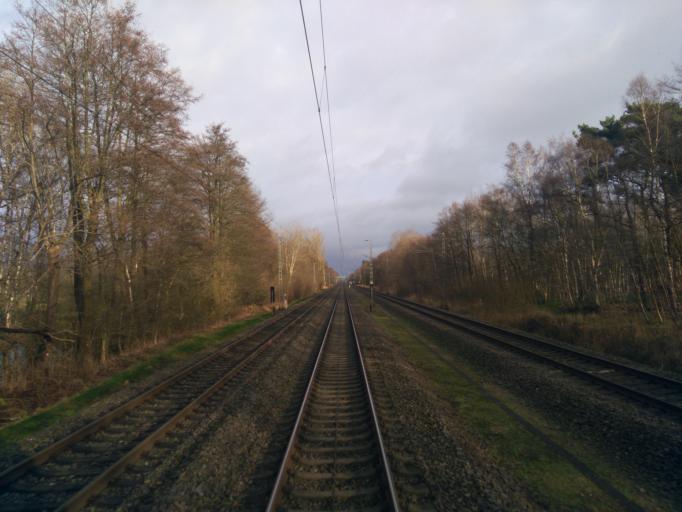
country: DE
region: Lower Saxony
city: Konigsmoor
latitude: 53.2451
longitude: 9.6737
